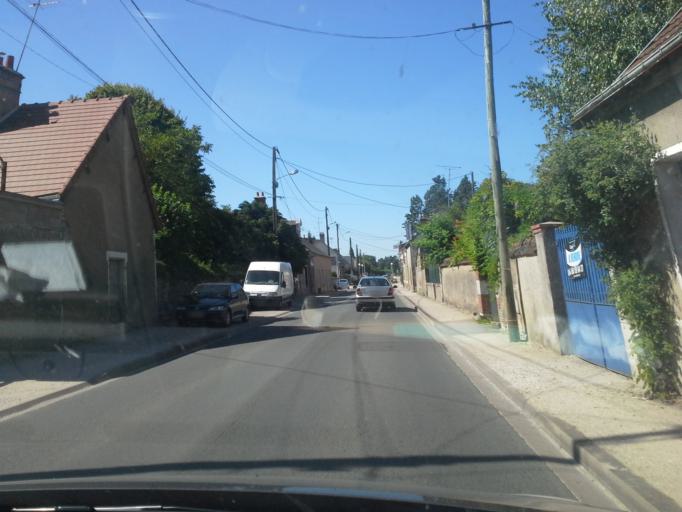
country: FR
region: Centre
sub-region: Departement du Loir-et-Cher
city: Cormeray
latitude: 47.4906
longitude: 1.4069
